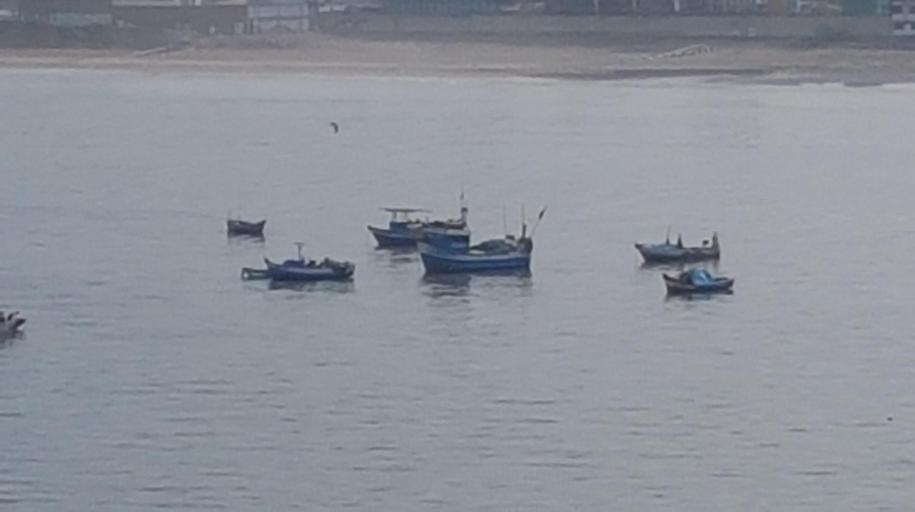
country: PE
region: Lima
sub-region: Barranca
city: Puerto Supe
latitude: -10.8000
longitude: -77.7503
